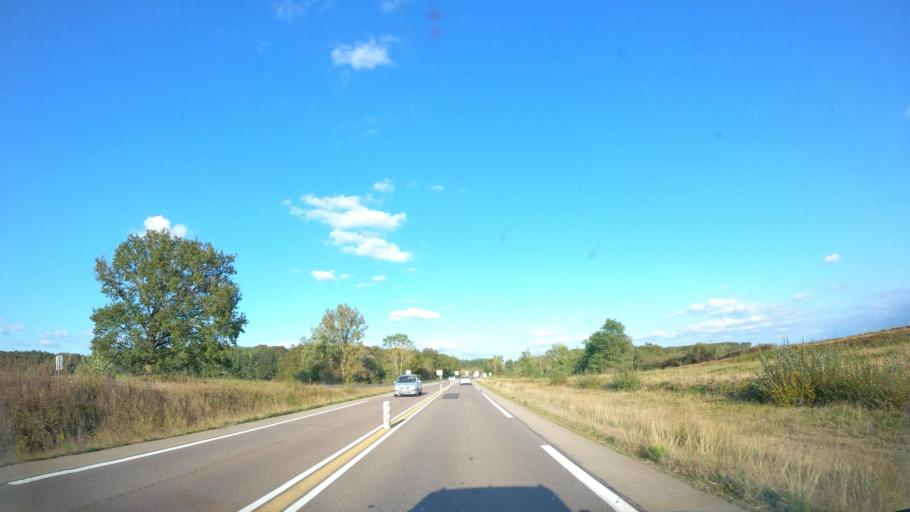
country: FR
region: Bourgogne
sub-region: Departement de Saone-et-Loire
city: Genelard
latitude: 46.6053
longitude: 4.2508
